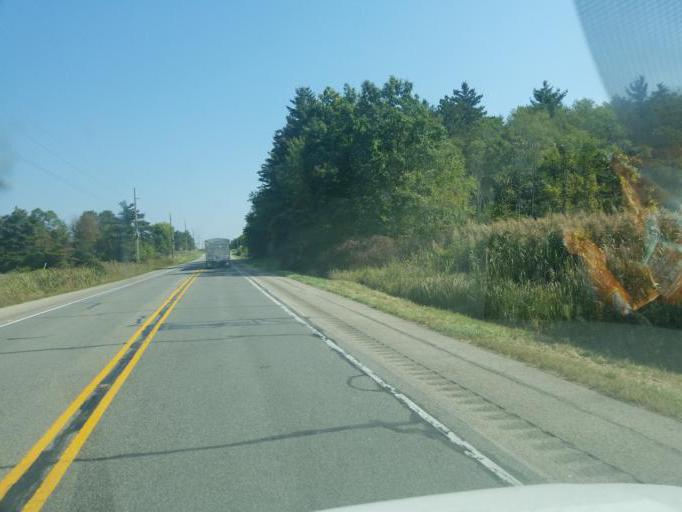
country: US
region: Indiana
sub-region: Steuben County
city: Angola
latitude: 41.6428
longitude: -85.1927
